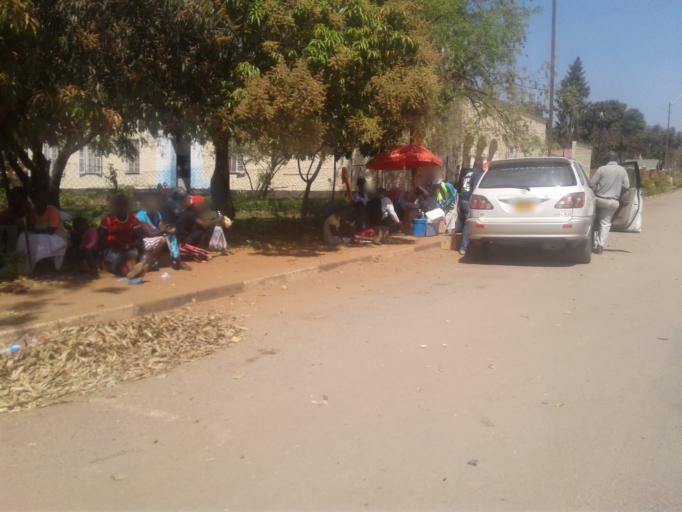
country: ZW
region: Mashonaland West
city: Chinhoyi
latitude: -17.3610
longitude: 30.1940
